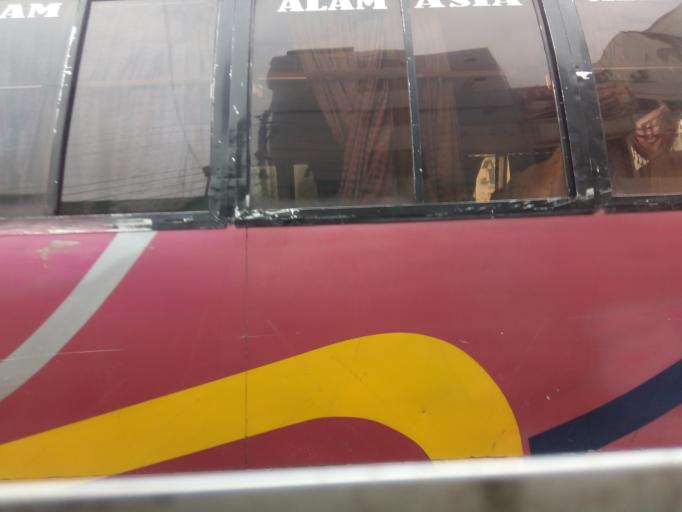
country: BD
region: Dhaka
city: Paltan
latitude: 23.7941
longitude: 90.4006
